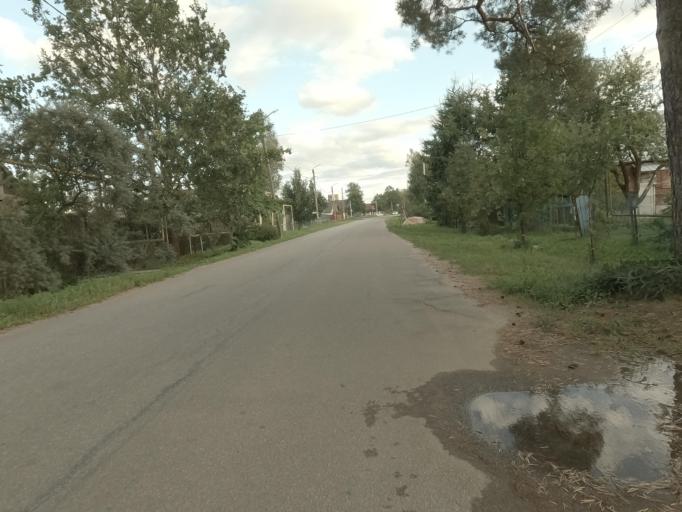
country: RU
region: Leningrad
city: Mga
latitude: 59.7585
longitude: 31.0765
